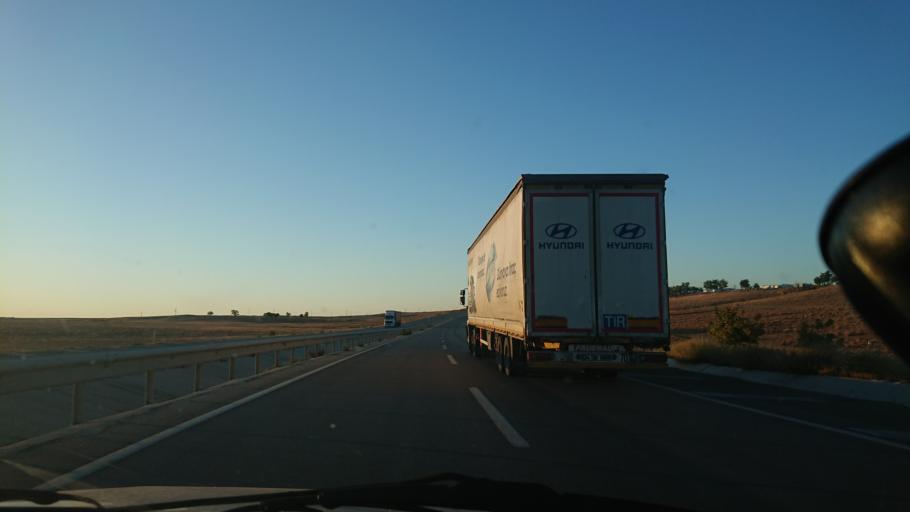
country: TR
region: Eskisehir
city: Mahmudiye
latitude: 39.4994
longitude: 30.9691
